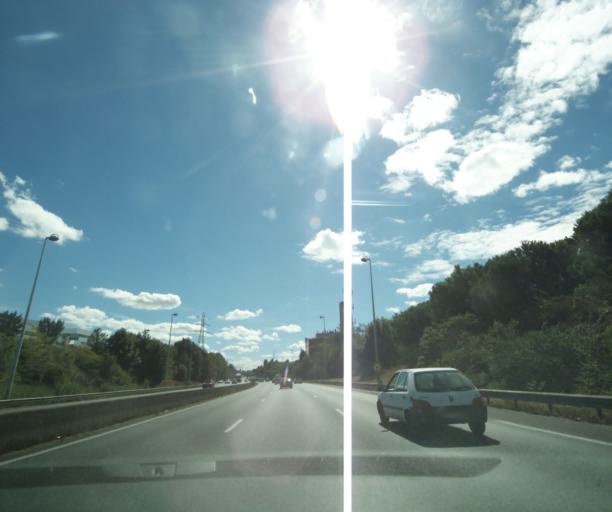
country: FR
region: Aquitaine
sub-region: Departement de la Gironde
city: Artigues-pres-Bordeaux
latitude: 44.8532
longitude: -0.5052
